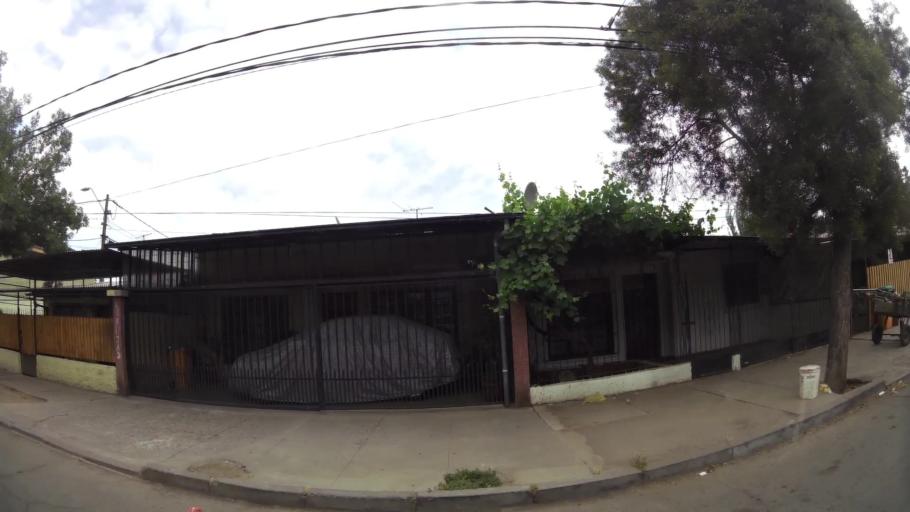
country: CL
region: Santiago Metropolitan
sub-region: Provincia de Santiago
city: Santiago
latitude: -33.5120
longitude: -70.6895
